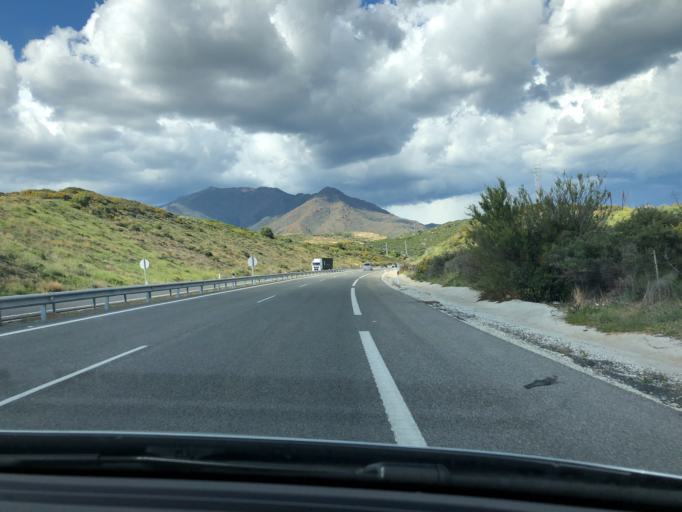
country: ES
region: Andalusia
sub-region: Provincia de Malaga
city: Manilva
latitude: 36.4179
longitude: -5.2203
